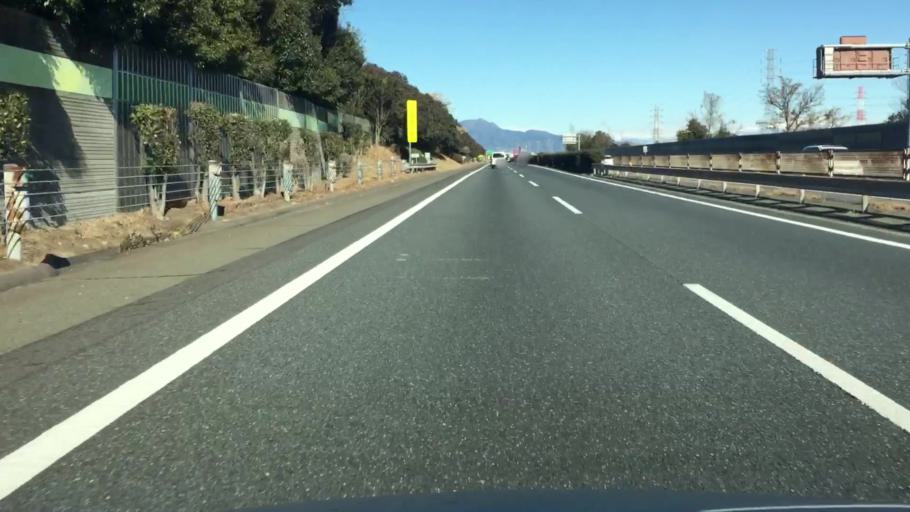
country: JP
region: Gunma
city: Maebashi-shi
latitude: 36.3799
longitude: 139.0270
